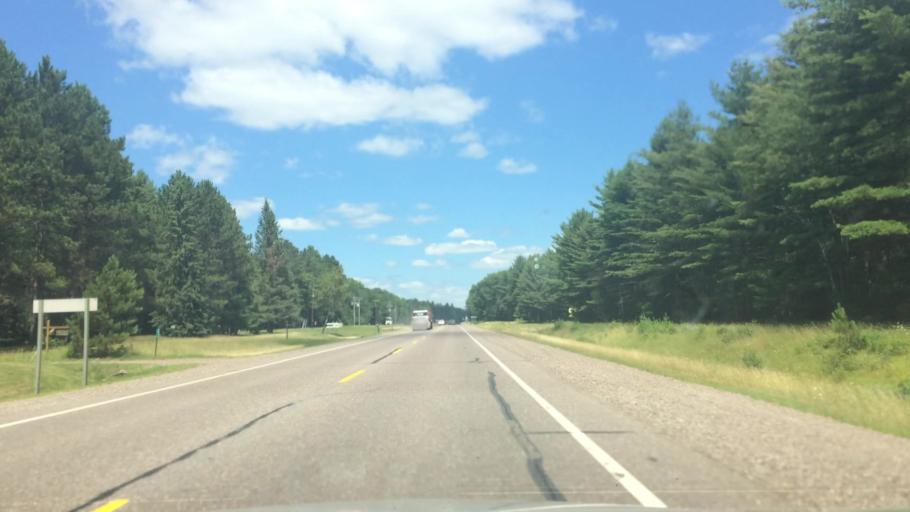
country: US
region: Wisconsin
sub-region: Vilas County
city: Lac du Flambeau
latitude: 45.9756
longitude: -89.6992
